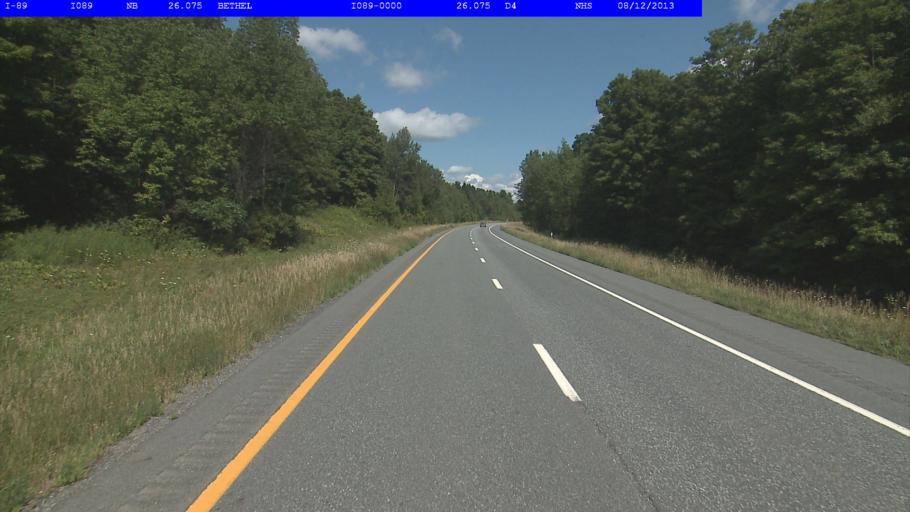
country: US
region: Vermont
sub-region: Orange County
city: Randolph
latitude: 43.8761
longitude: -72.6137
